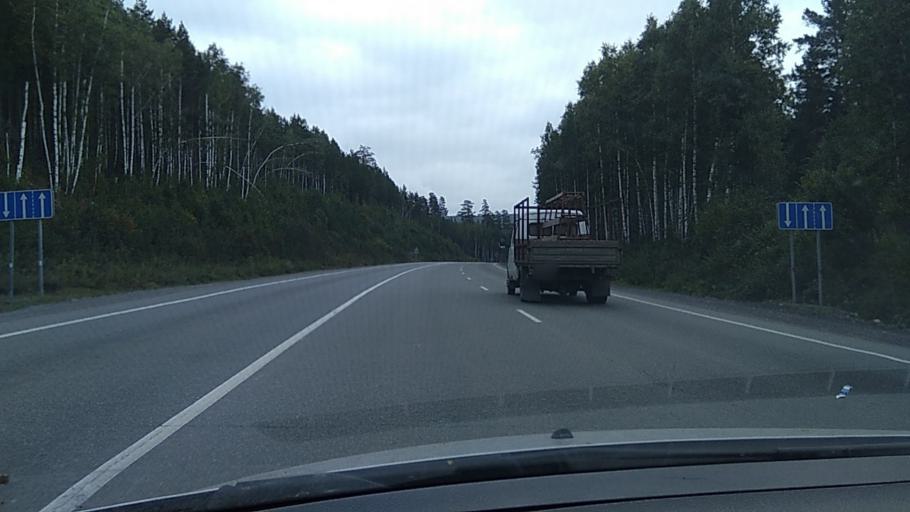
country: RU
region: Chelyabinsk
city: Zlatoust
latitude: 55.0538
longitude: 59.7140
